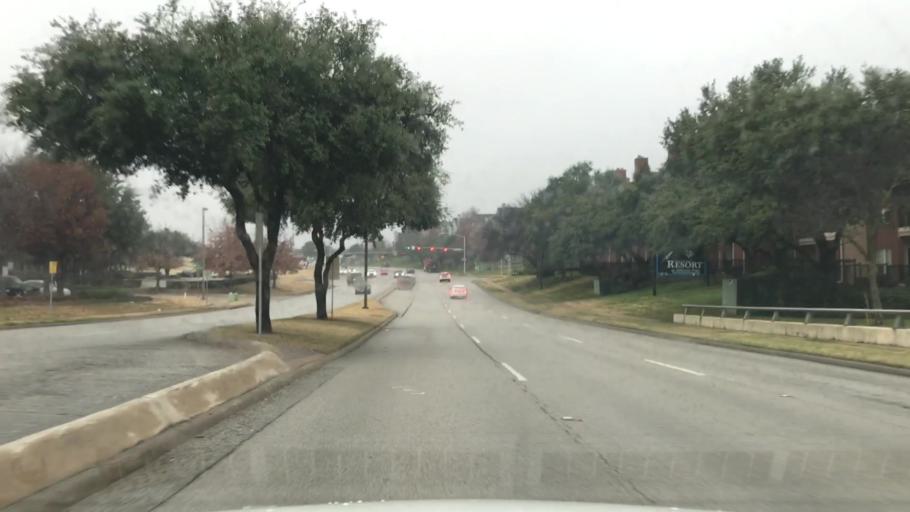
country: US
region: Texas
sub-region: Dallas County
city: Irving
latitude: 32.8787
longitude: -96.9632
